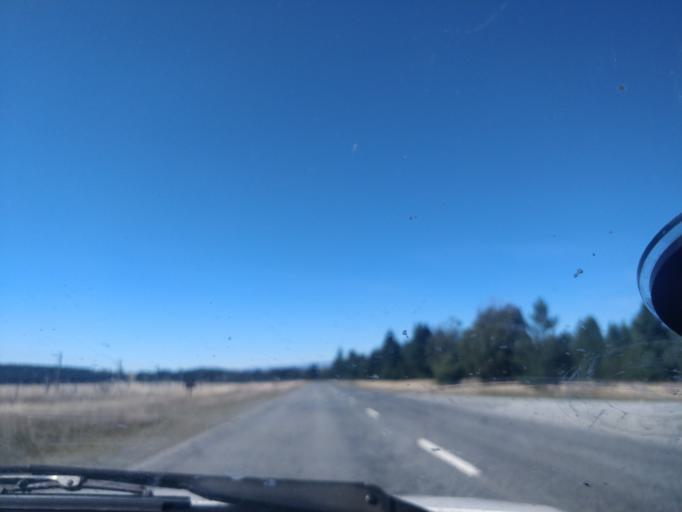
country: NZ
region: Otago
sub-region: Queenstown-Lakes District
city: Wanaka
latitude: -44.2722
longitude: 170.0517
